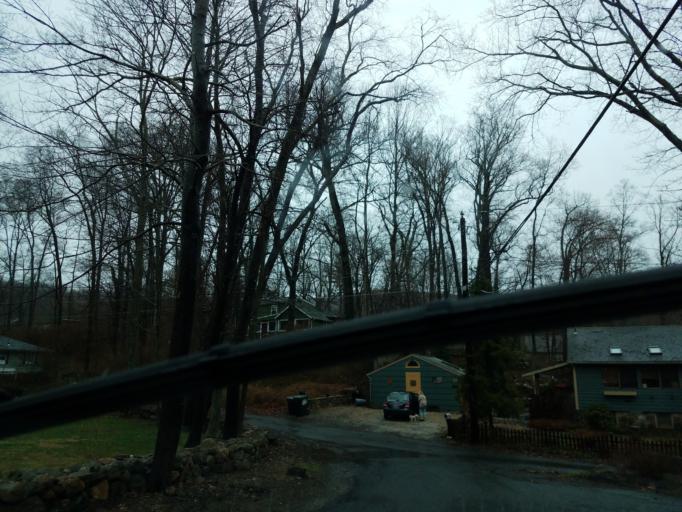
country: US
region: Connecticut
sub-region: Fairfield County
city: Ridgefield
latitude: 41.3409
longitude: -73.4911
